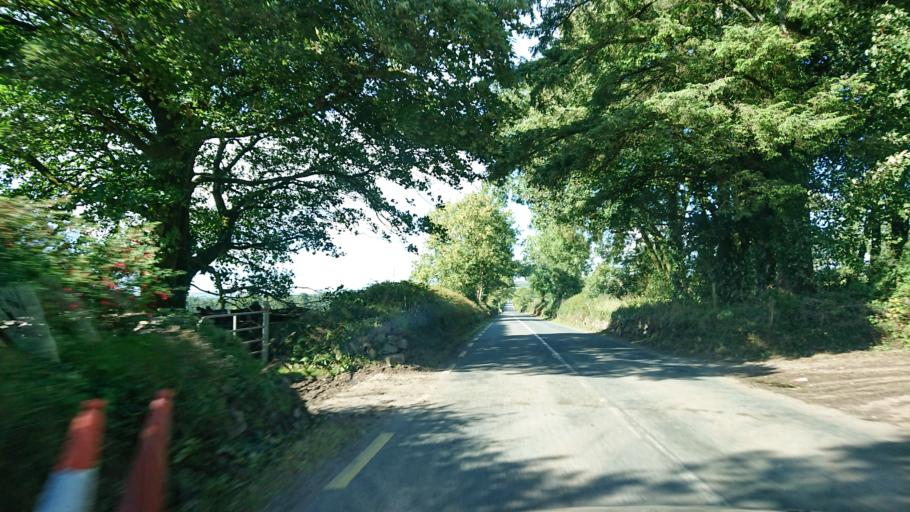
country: IE
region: Munster
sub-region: Waterford
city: Dungarvan
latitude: 52.1961
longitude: -7.6993
